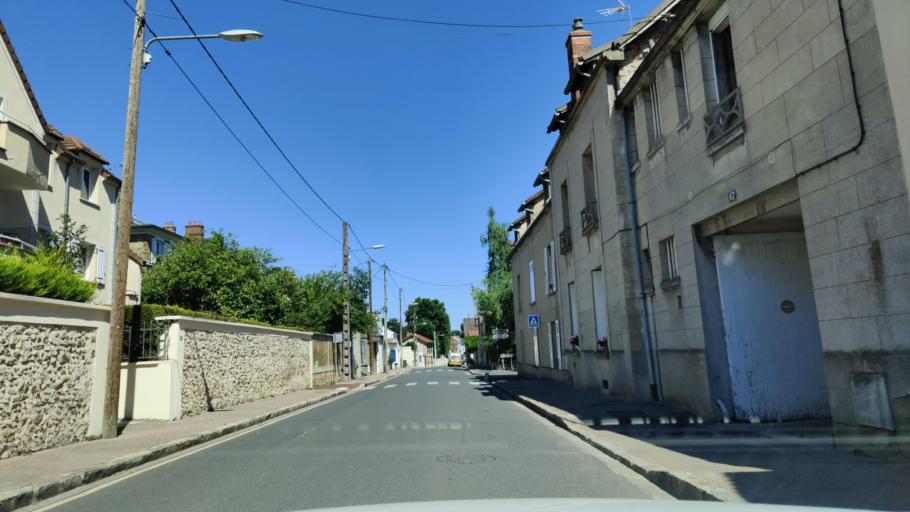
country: FR
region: Ile-de-France
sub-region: Departement de l'Essonne
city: Bruyeres-le-Chatel
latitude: 48.5927
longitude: 2.1873
